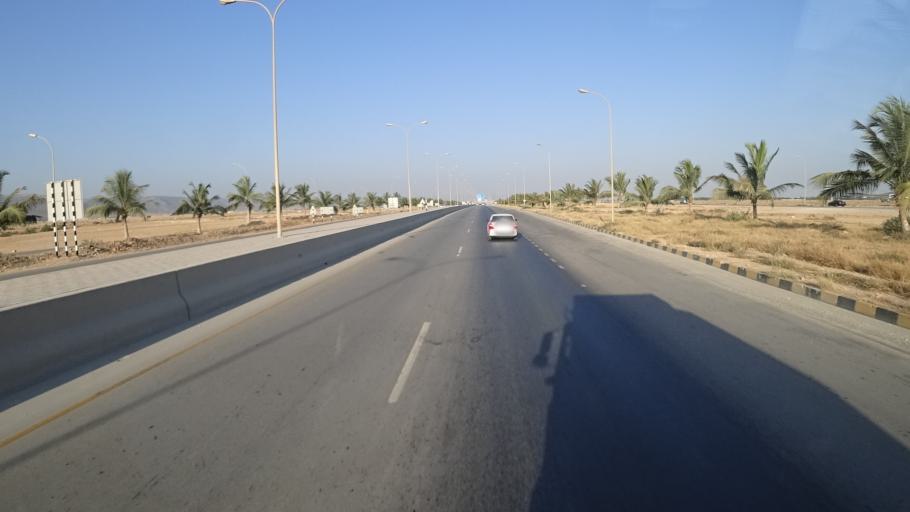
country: OM
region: Zufar
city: Salalah
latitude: 17.0495
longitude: 54.0655
